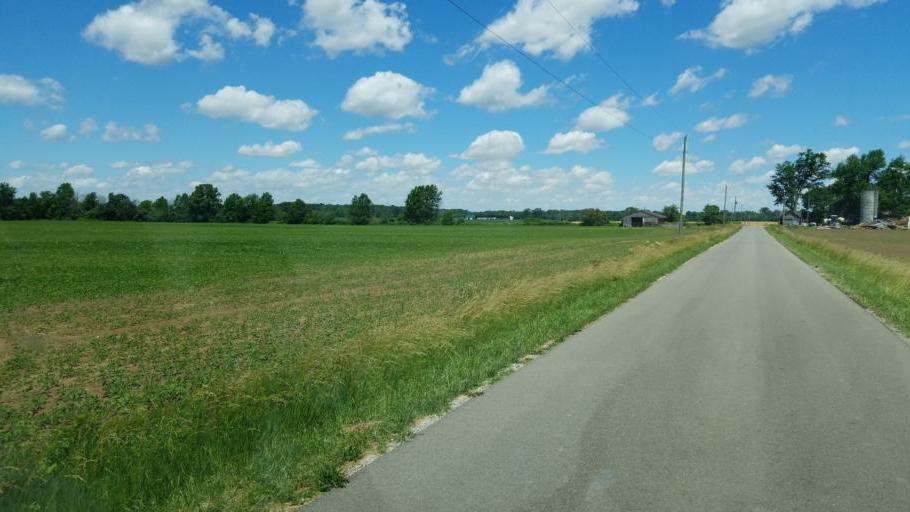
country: US
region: Ohio
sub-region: Crawford County
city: Galion
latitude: 40.7272
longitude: -82.8654
